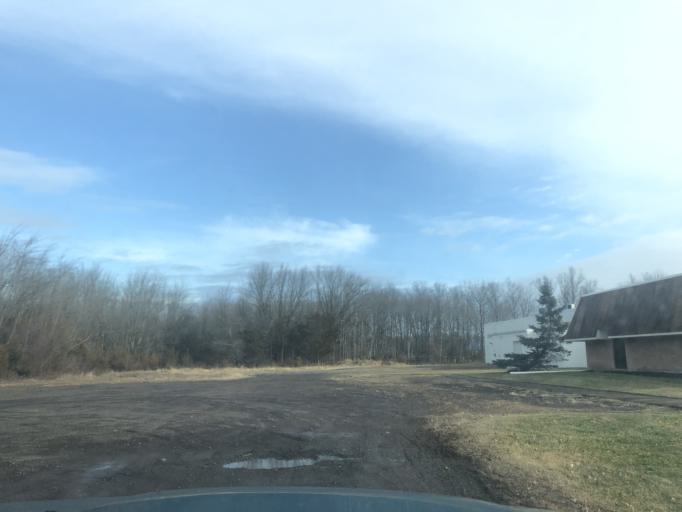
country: US
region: Pennsylvania
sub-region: Bucks County
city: Perkasie
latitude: 40.3820
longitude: -75.2968
